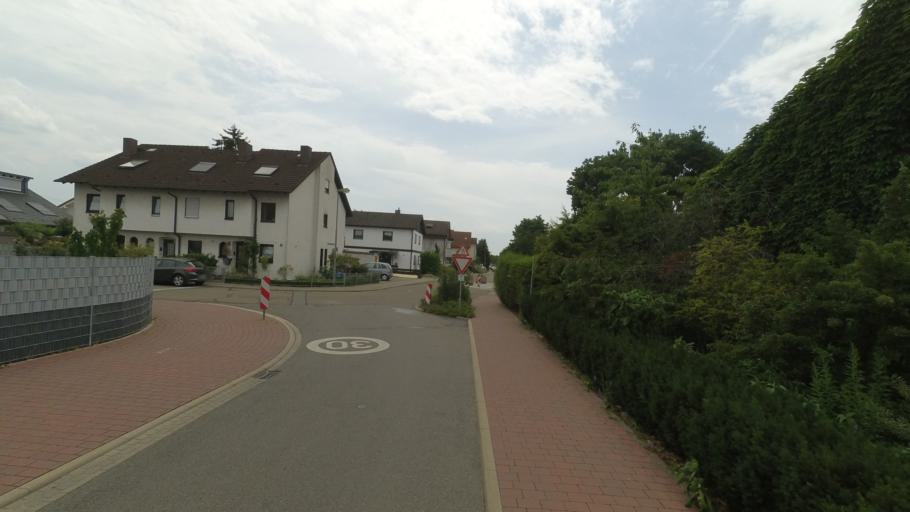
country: DE
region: Baden-Wuerttemberg
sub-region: Karlsruhe Region
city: Bruhl
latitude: 49.3993
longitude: 8.5393
